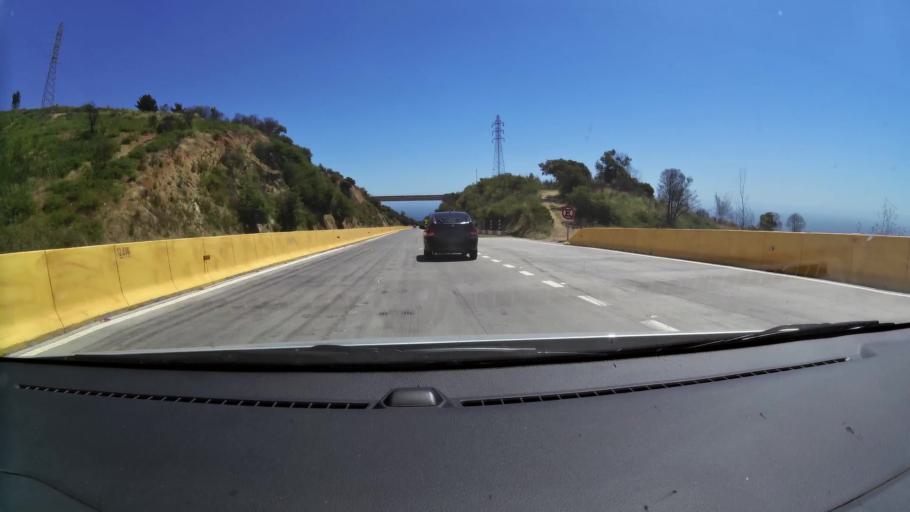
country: CL
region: Valparaiso
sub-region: Provincia de Valparaiso
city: Valparaiso
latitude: -33.0584
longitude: -71.6498
